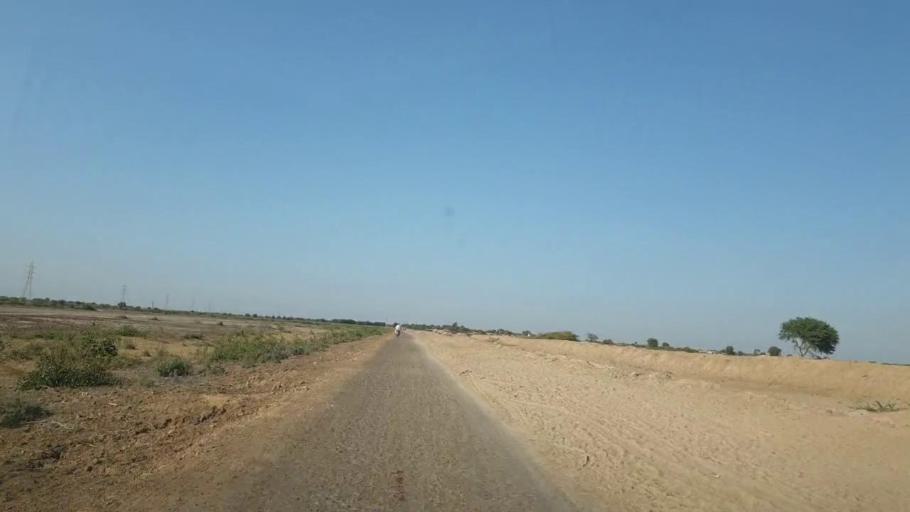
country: PK
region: Sindh
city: Naukot
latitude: 25.0387
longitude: 69.4421
